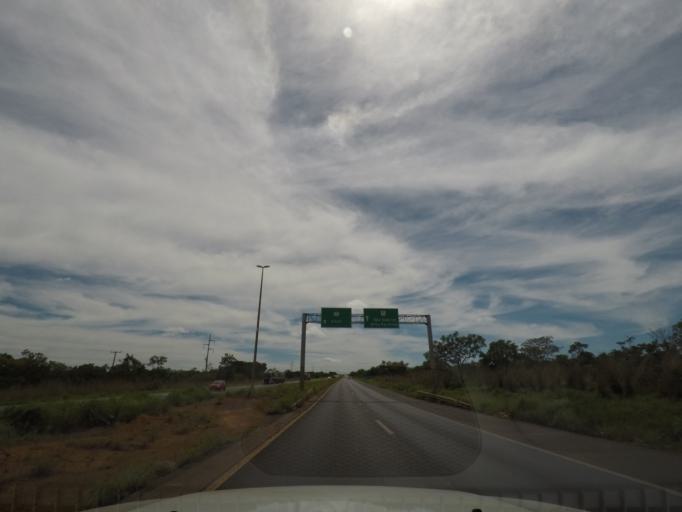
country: BR
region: Goias
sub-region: Planaltina
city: Planaltina
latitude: -15.5956
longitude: -47.6494
